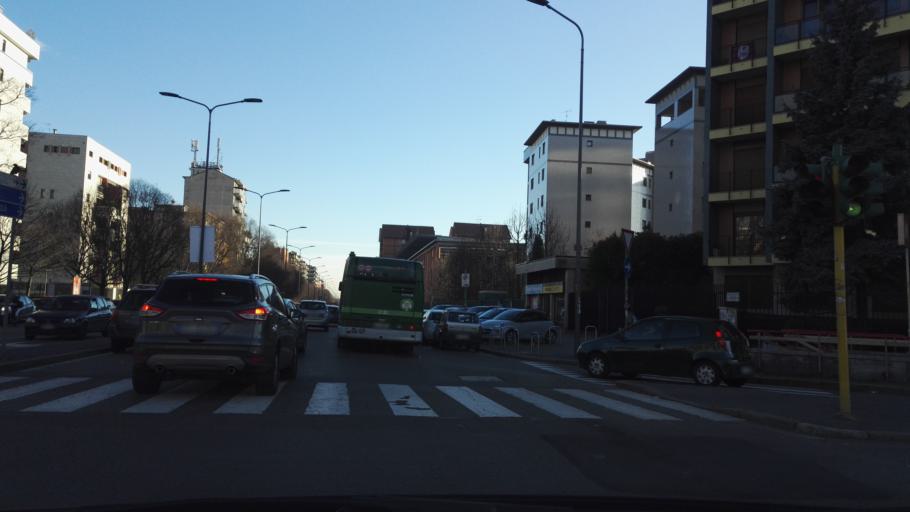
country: IT
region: Lombardy
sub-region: Citta metropolitana di Milano
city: Romano Banco
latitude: 45.4595
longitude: 9.1296
